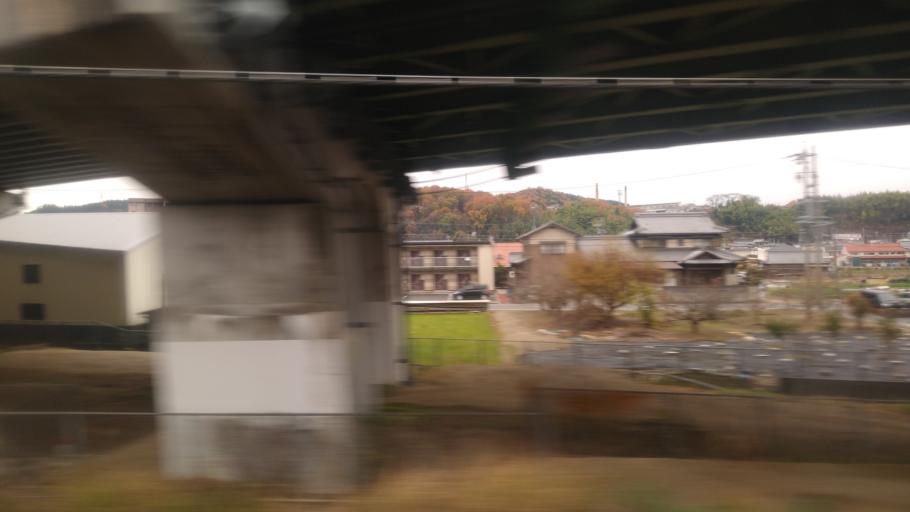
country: JP
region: Gifu
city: Mizunami
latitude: 35.3647
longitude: 137.2263
